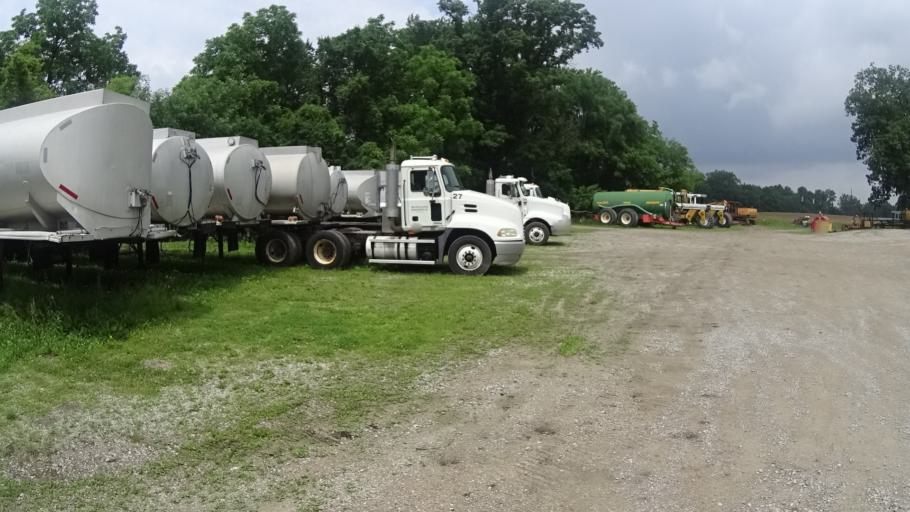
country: US
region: Ohio
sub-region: Huron County
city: Bellevue
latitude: 41.3281
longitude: -82.8197
